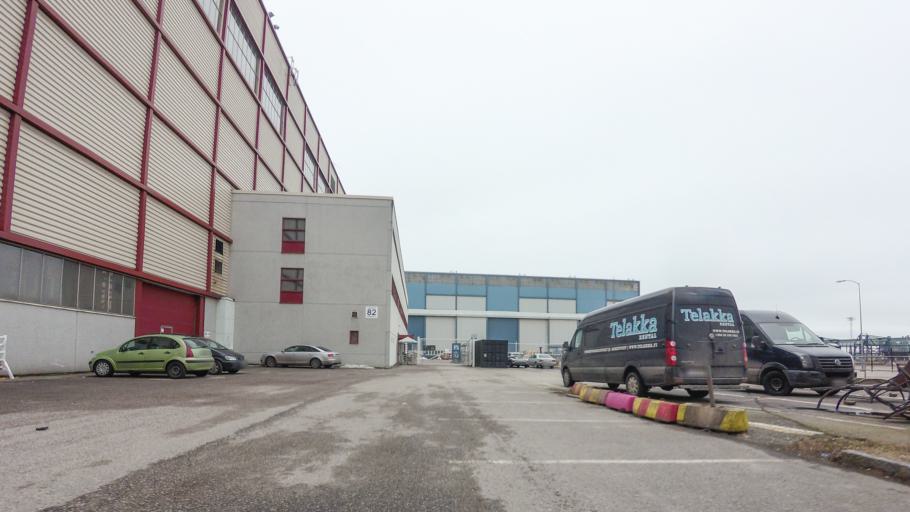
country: FI
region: Uusimaa
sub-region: Helsinki
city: Helsinki
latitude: 60.1520
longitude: 24.9254
